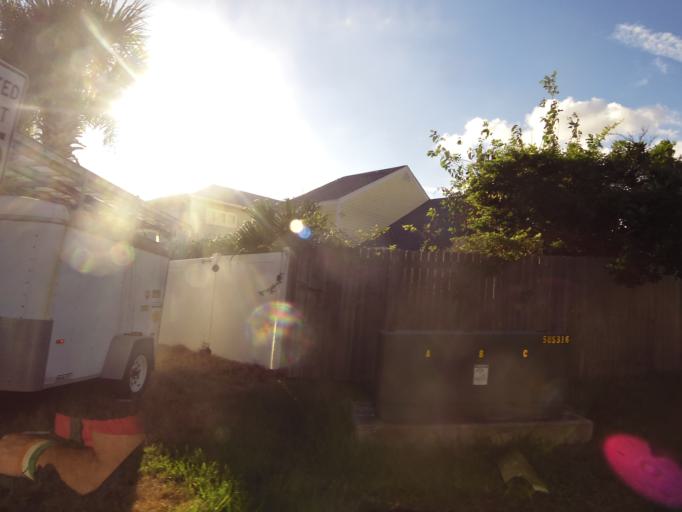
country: US
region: Florida
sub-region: Saint Johns County
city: Ponte Vedra Beach
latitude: 30.2667
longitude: -81.3864
